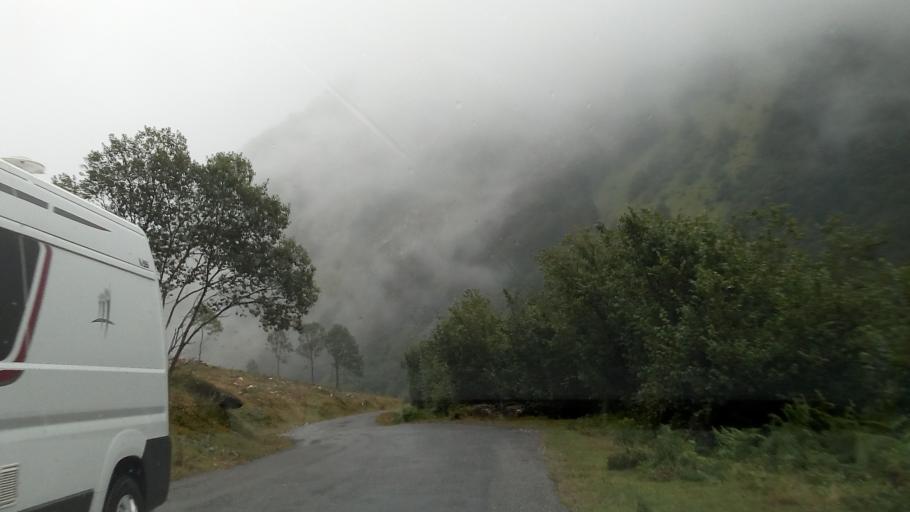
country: FR
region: Midi-Pyrenees
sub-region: Departement des Hautes-Pyrenees
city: Cauterets
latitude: 42.9234
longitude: -0.2512
